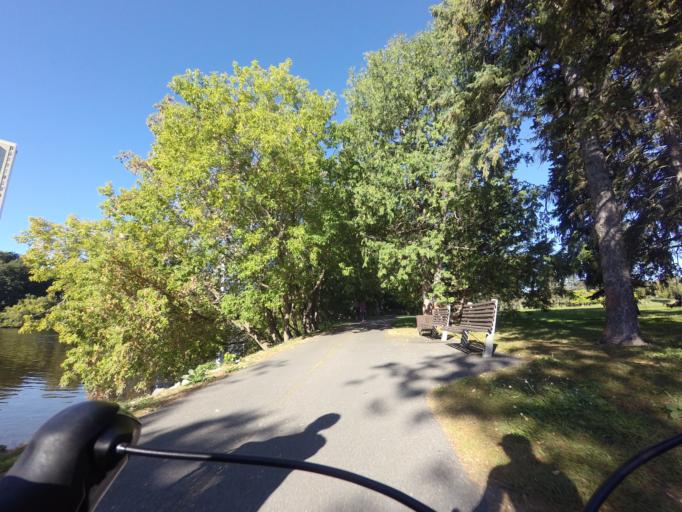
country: CA
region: Ontario
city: Ottawa
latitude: 45.4357
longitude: -75.6732
